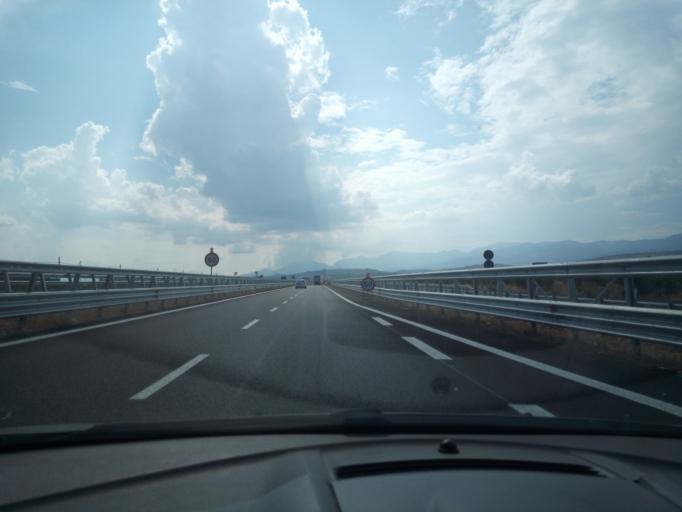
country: IT
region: Calabria
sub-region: Provincia di Cosenza
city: San Lorenzo del Vallo
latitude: 39.7247
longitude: 16.2591
